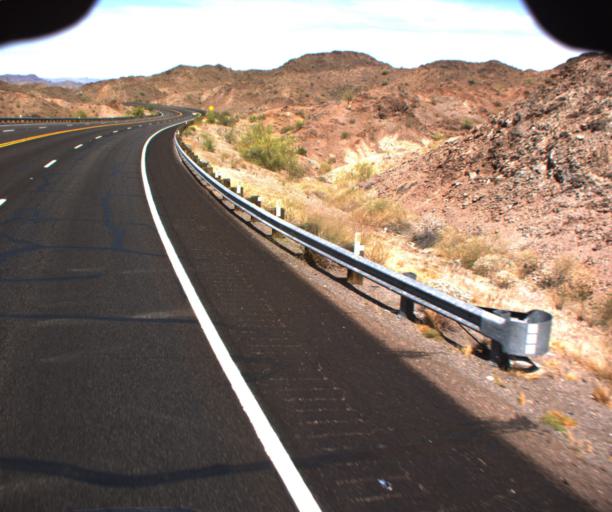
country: US
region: Arizona
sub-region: La Paz County
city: Cienega Springs
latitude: 34.2000
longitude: -114.2095
